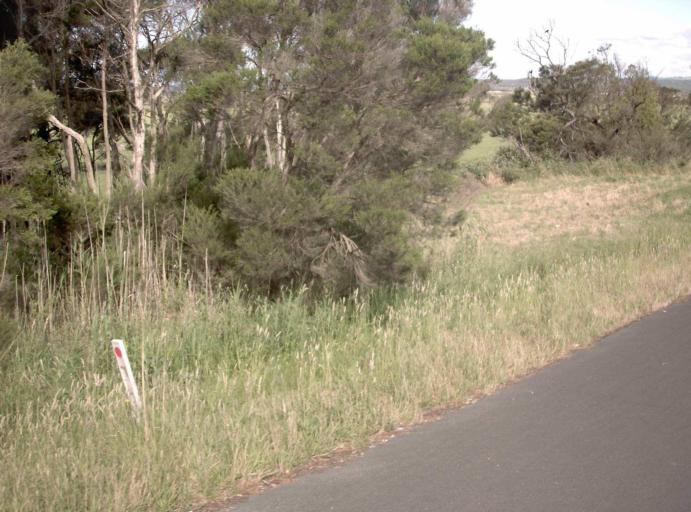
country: AU
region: Victoria
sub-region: Cardinia
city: Koo-Wee-Rup
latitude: -38.3222
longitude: 145.5413
